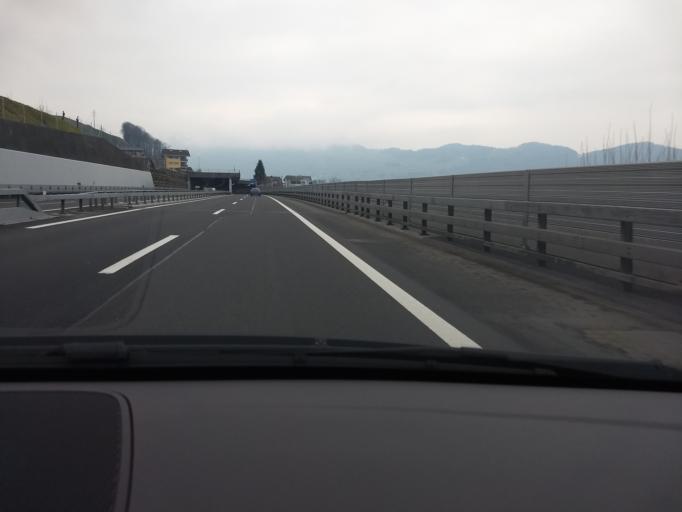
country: CH
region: Nidwalden
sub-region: Nidwalden
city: Beckenried
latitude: 46.9657
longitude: 8.4641
